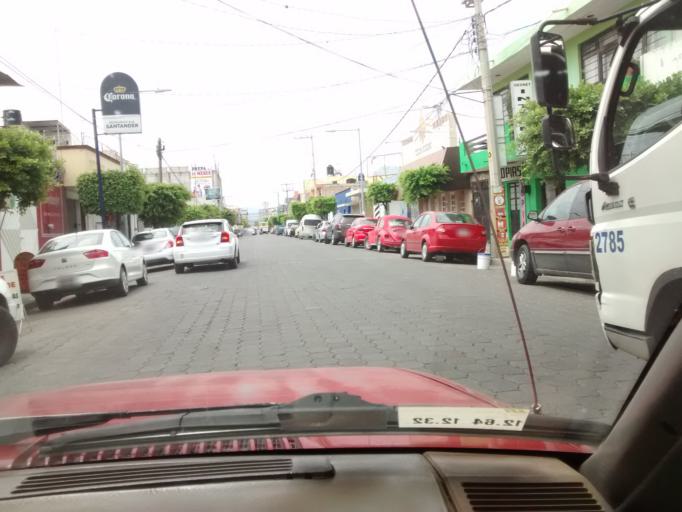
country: MX
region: Puebla
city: Tehuacan
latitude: 18.4647
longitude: -97.3980
